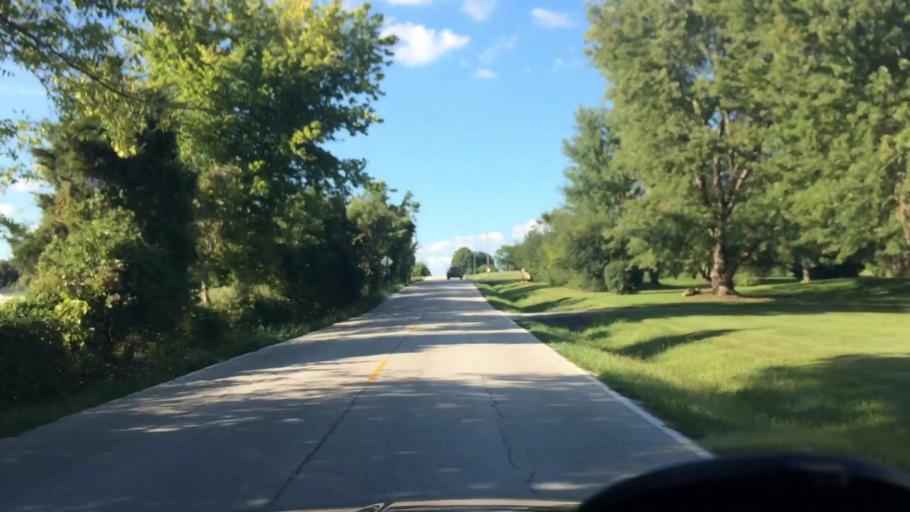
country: US
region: Missouri
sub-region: Greene County
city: Strafford
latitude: 37.2783
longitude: -93.0812
